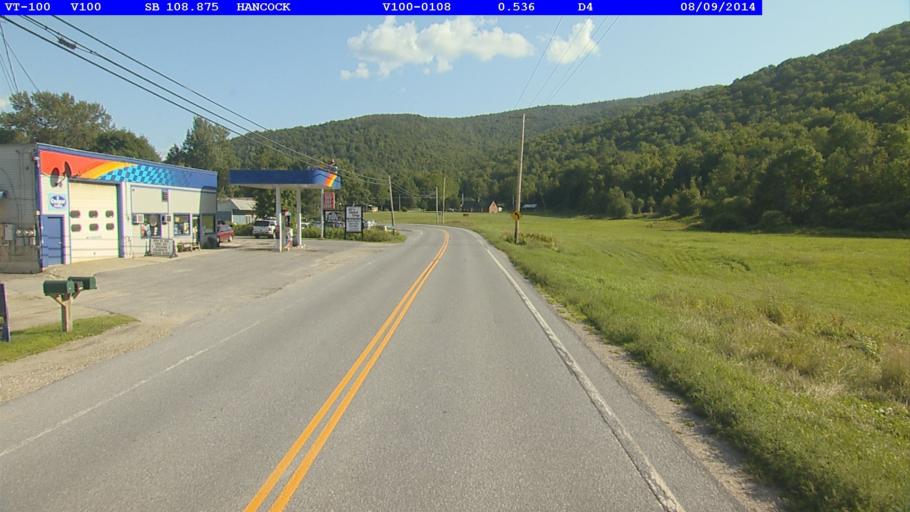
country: US
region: Vermont
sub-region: Orange County
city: Randolph
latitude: 43.9168
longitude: -72.8408
